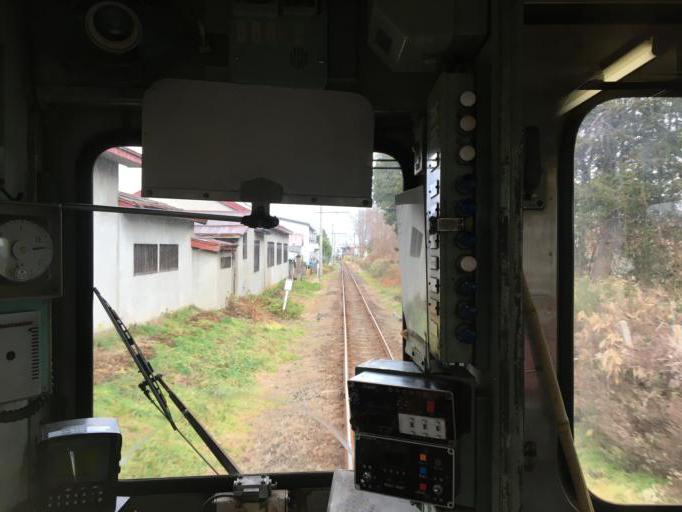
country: JP
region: Aomori
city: Hirosaki
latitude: 40.5784
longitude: 140.4723
